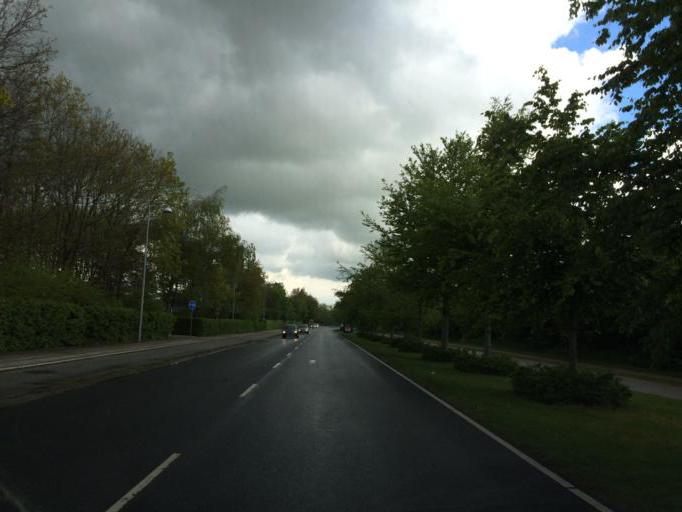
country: DK
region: Central Jutland
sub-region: Holstebro Kommune
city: Holstebro
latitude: 56.3711
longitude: 8.6111
